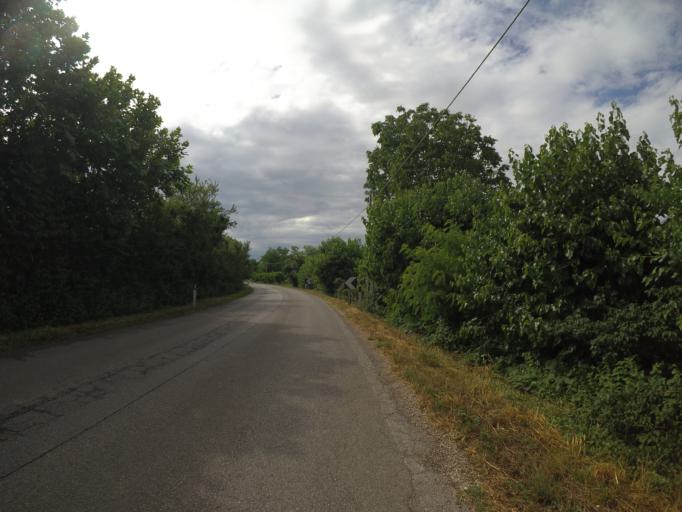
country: IT
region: Friuli Venezia Giulia
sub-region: Provincia di Udine
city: Lestizza
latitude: 45.9600
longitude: 13.1298
